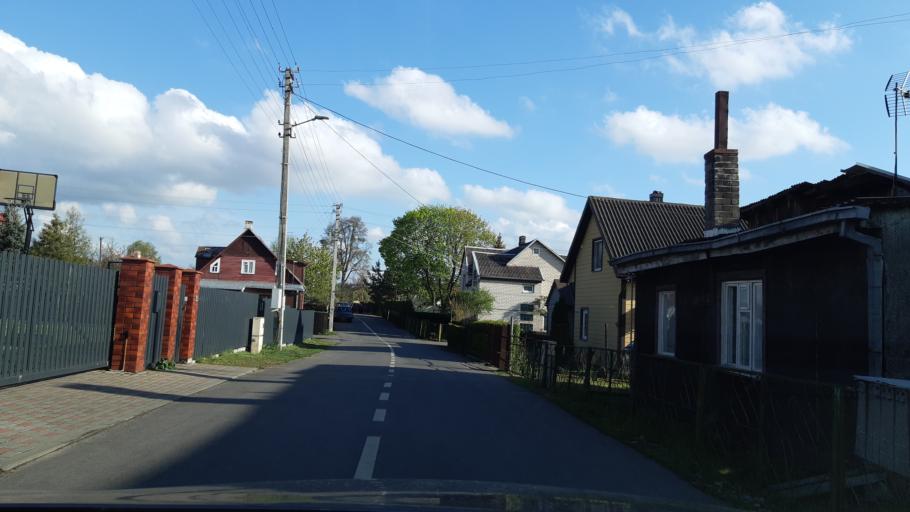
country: LT
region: Kauno apskritis
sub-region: Kaunas
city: Aleksotas
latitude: 54.8666
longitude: 23.9322
